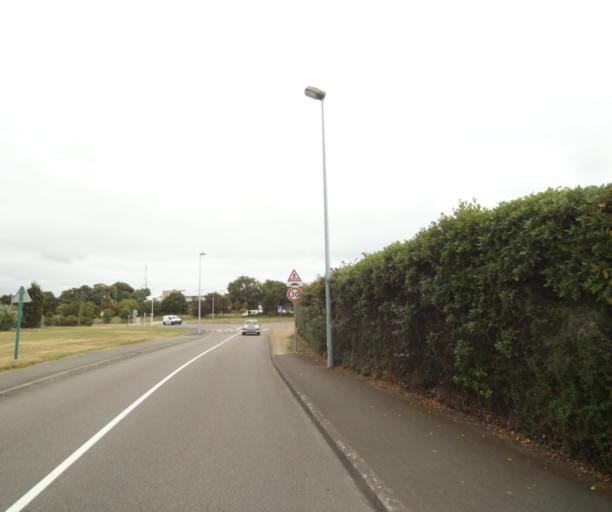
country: FR
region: Pays de la Loire
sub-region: Departement de la Vendee
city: Chateau-d'Olonne
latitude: 46.4928
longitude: -1.7469
